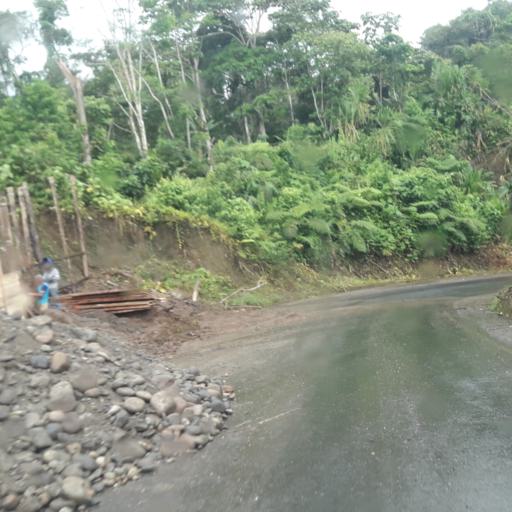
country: EC
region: Napo
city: Tena
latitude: -1.0381
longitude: -77.6663
